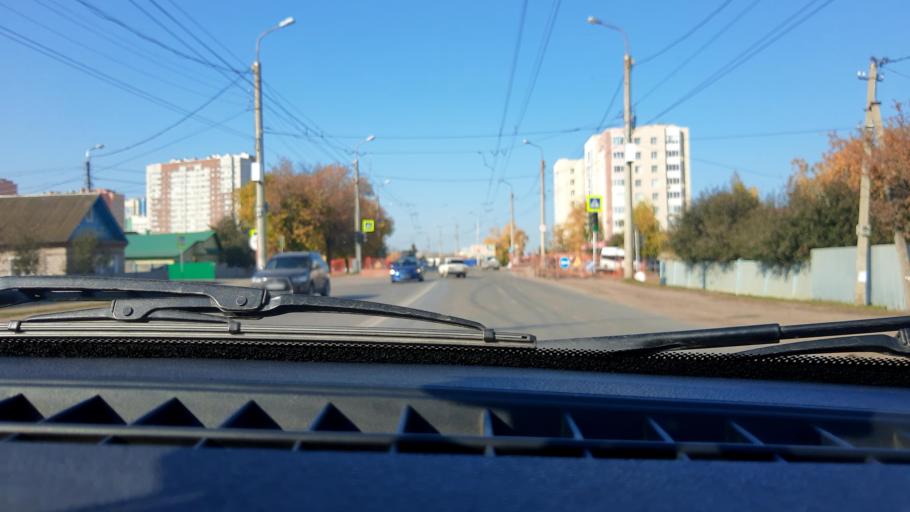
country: RU
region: Bashkortostan
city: Mikhaylovka
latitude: 54.7930
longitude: 55.8760
